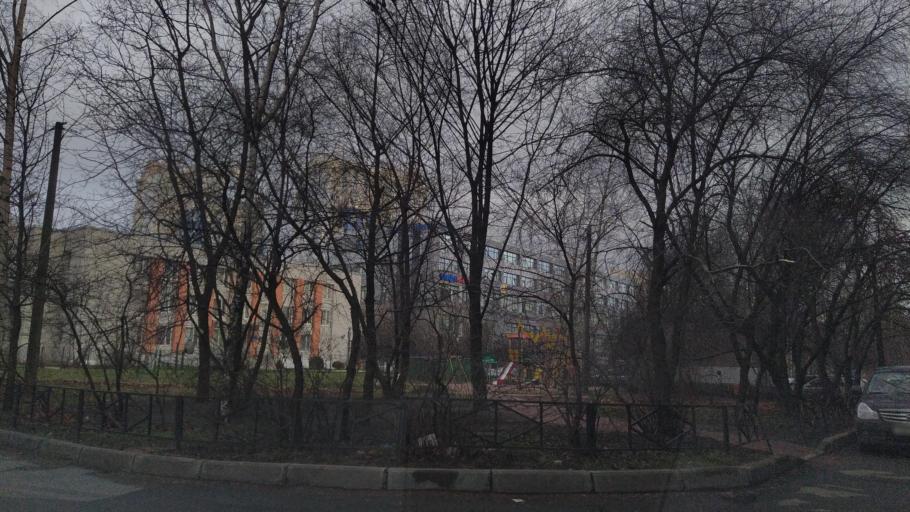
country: RU
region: St.-Petersburg
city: Centralniy
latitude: 59.9310
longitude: 30.4190
